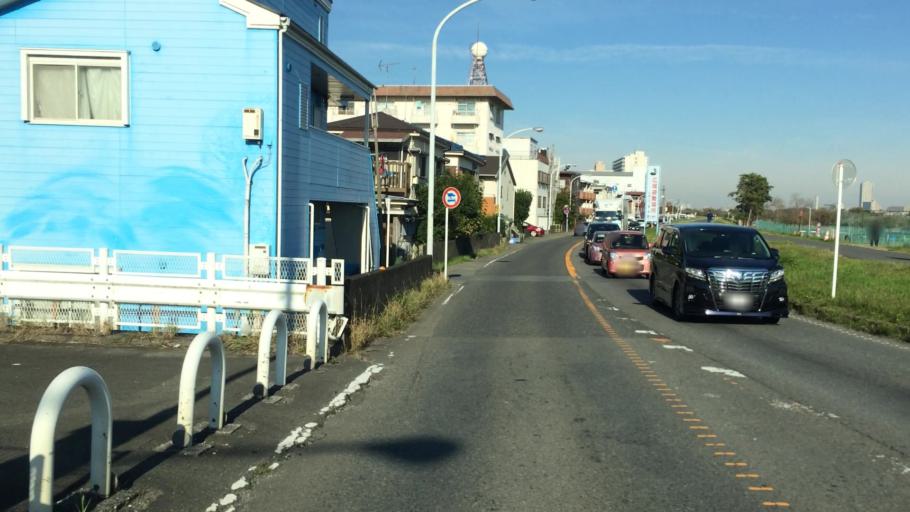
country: JP
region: Tokyo
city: Chofugaoka
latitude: 35.6247
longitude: 139.5666
